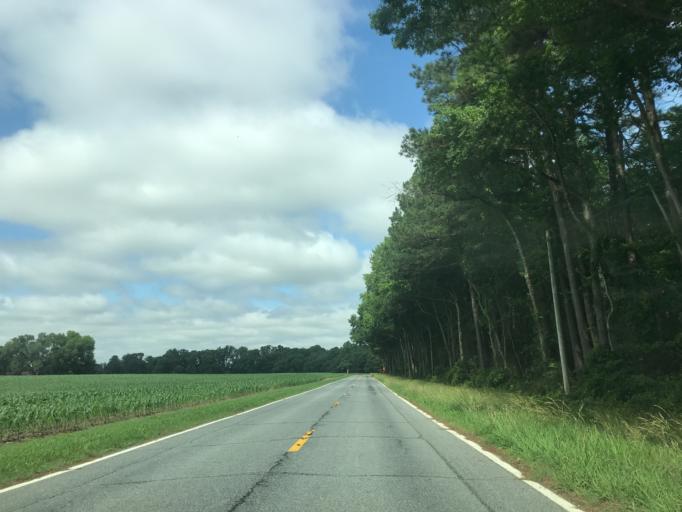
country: US
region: Maryland
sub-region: Caroline County
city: Ridgely
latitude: 38.9160
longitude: -75.9031
